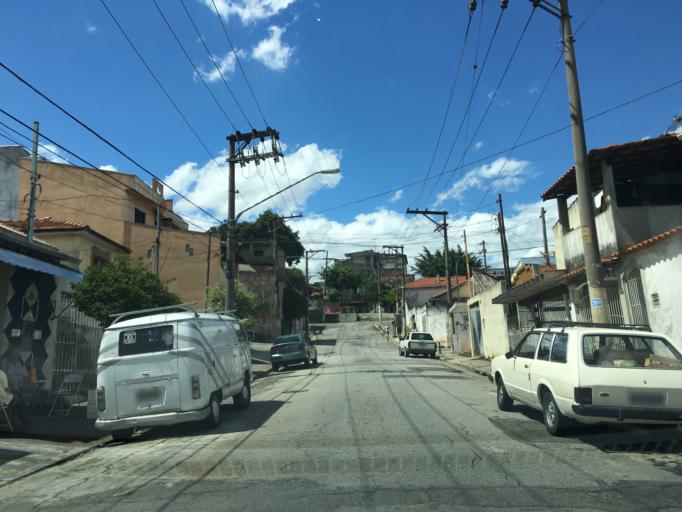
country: BR
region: Sao Paulo
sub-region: Sao Caetano Do Sul
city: Sao Caetano do Sul
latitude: -23.5749
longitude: -46.5623
